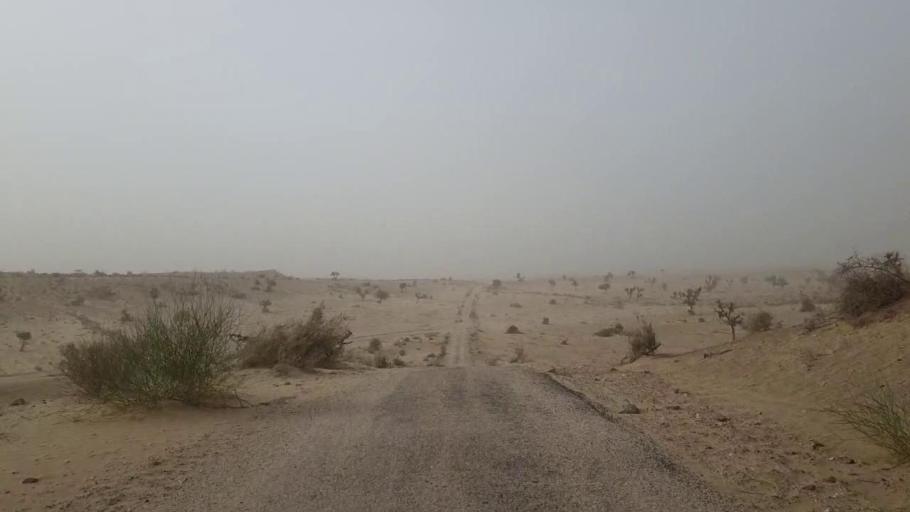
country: PK
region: Sindh
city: Islamkot
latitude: 24.5614
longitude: 70.3625
